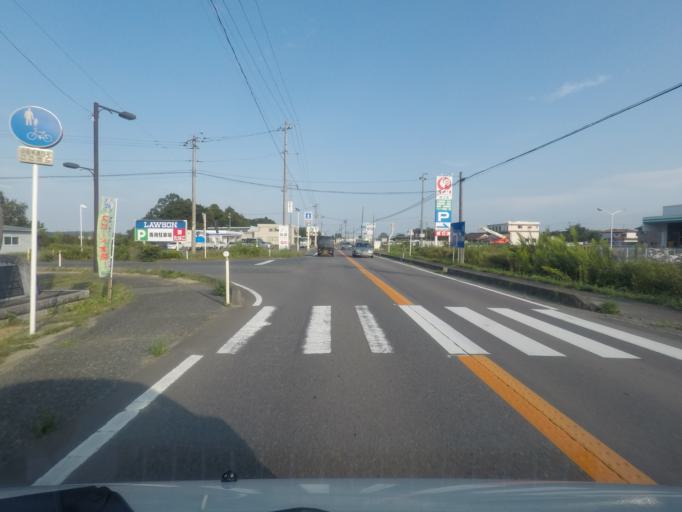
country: JP
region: Fukushima
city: Namie
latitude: 37.4971
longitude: 140.9704
